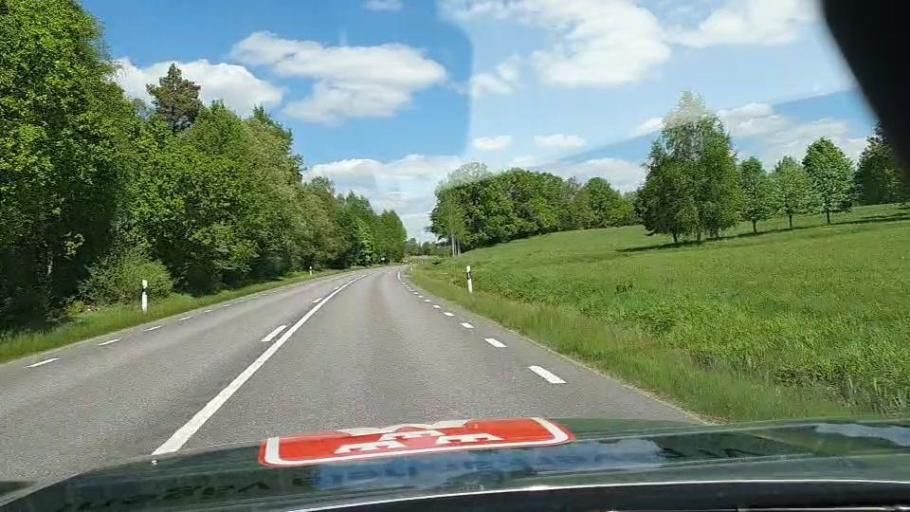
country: SE
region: Kronoberg
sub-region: Alvesta Kommun
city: Moheda
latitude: 57.0325
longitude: 14.5632
